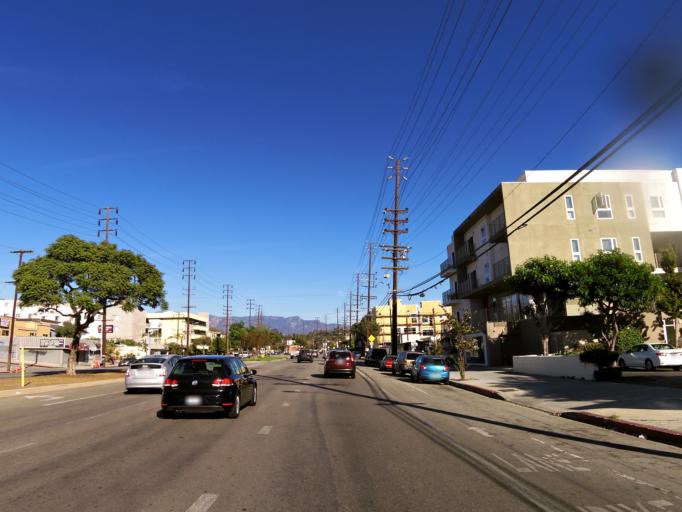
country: US
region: California
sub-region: Los Angeles County
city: Glendale
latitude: 34.1224
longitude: -118.2238
